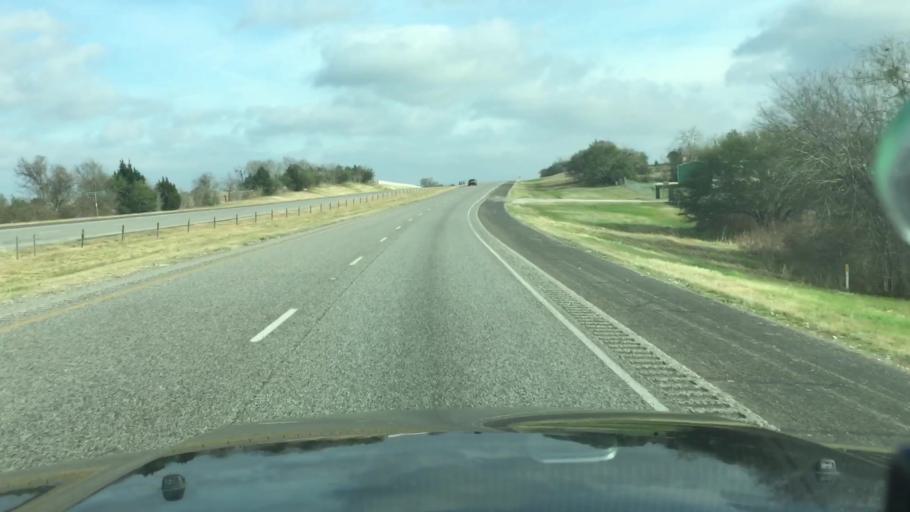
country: US
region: Texas
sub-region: Washington County
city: Brenham
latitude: 30.1353
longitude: -96.2515
